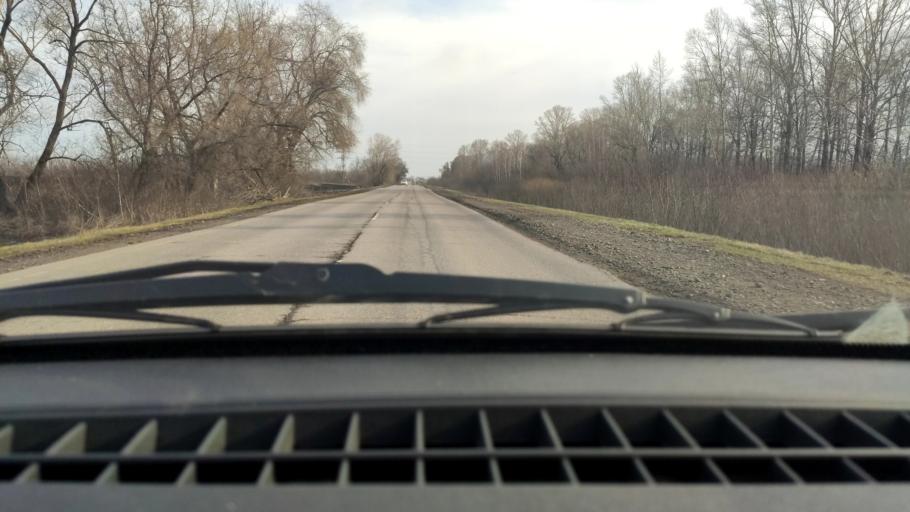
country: RU
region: Bashkortostan
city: Chishmy
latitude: 54.5172
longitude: 55.2958
